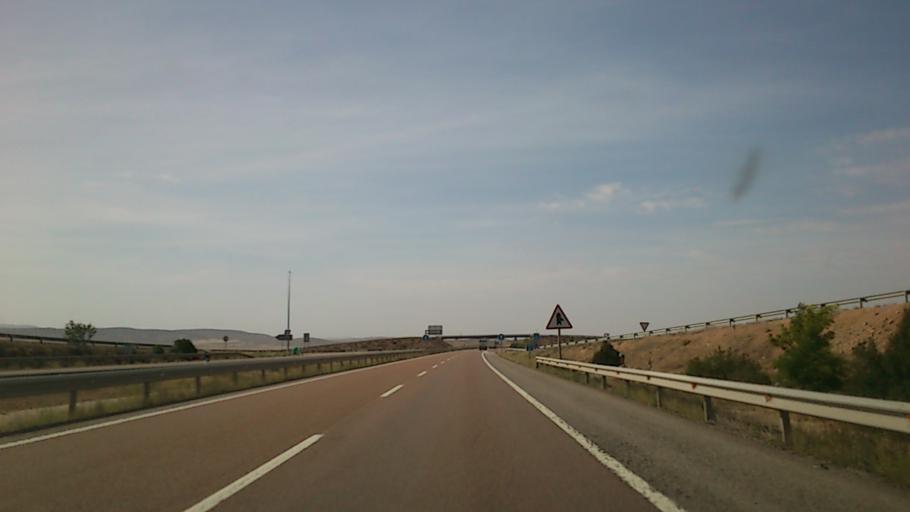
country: ES
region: Aragon
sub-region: Provincia de Teruel
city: Singra
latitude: 40.6225
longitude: -1.2986
